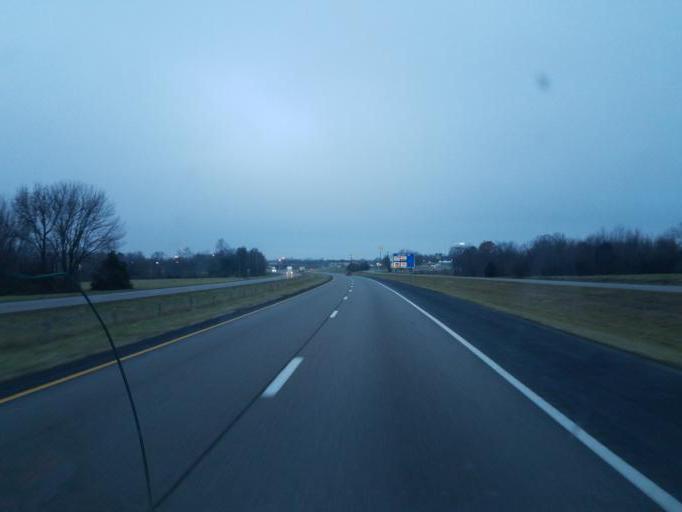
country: US
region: Missouri
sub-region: Phelps County
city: Saint James
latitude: 38.0082
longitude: -91.6123
